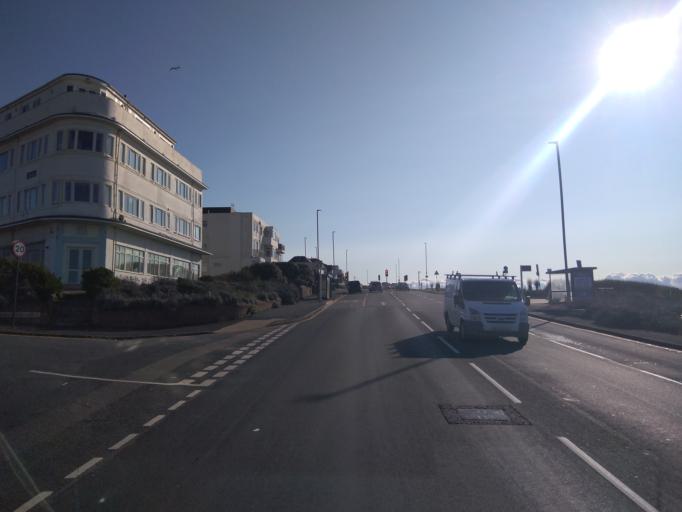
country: GB
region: England
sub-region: Brighton and Hove
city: Rottingdean
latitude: 50.8006
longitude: -0.0405
